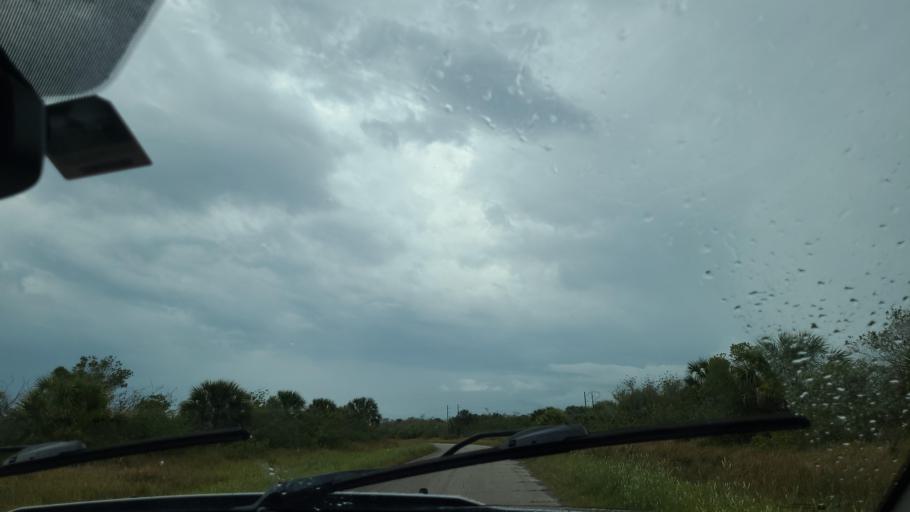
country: US
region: Florida
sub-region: Brevard County
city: June Park
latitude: 27.9482
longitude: -80.7093
